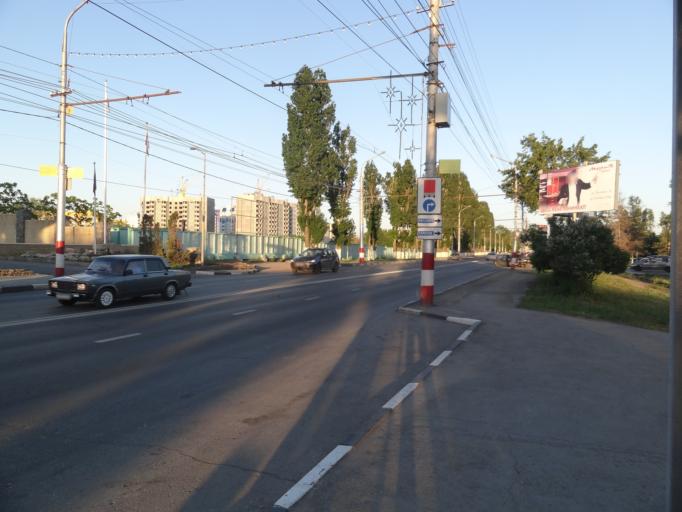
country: RU
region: Saratov
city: Engel's
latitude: 51.4971
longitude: 46.0895
